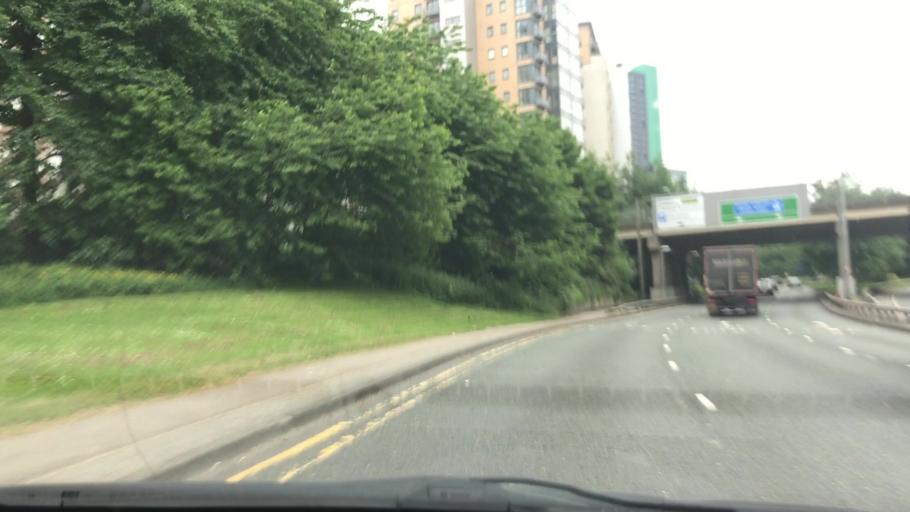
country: GB
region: England
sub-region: City and Borough of Leeds
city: Leeds
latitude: 53.8058
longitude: -1.5381
